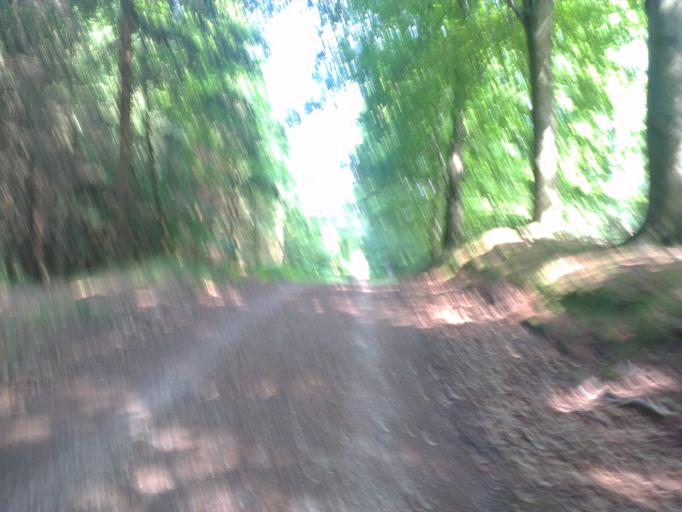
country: DK
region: Capital Region
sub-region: Allerod Kommune
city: Lillerod
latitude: 55.9081
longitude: 12.3575
